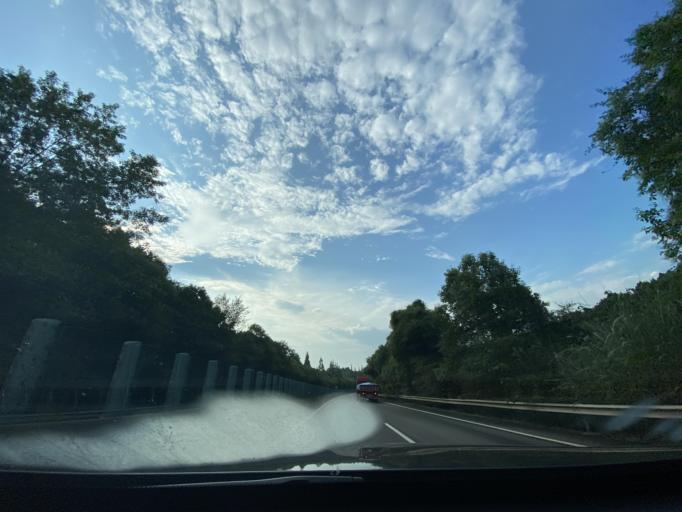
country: CN
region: Sichuan
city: Jiancheng
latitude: 30.3287
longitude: 104.5680
